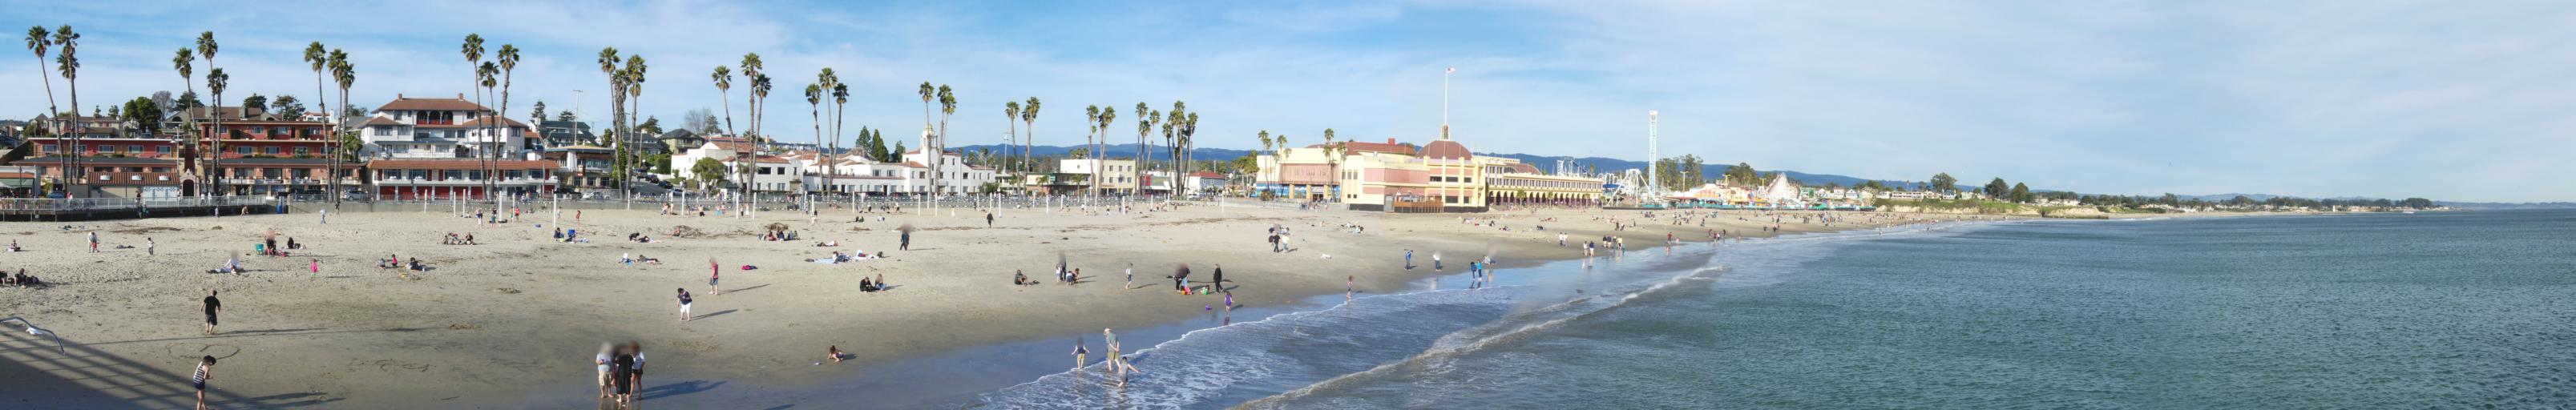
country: US
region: California
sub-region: Santa Cruz County
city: Santa Cruz
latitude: 36.9620
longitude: -122.0226
